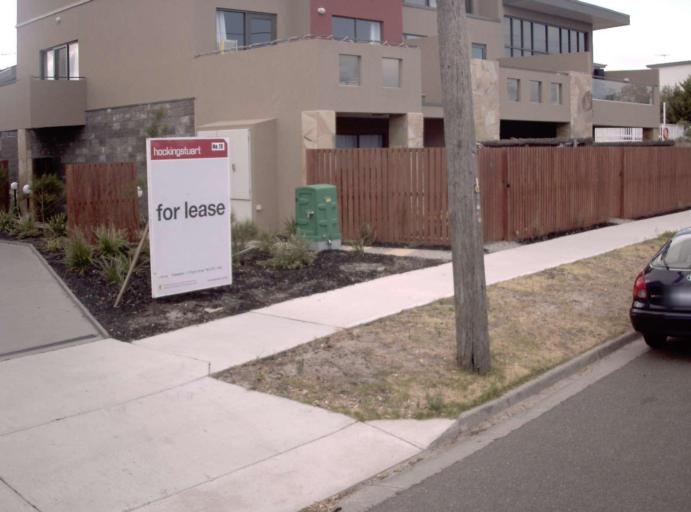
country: AU
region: Victoria
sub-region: Kingston
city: Carrum
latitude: -38.0902
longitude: 145.1253
